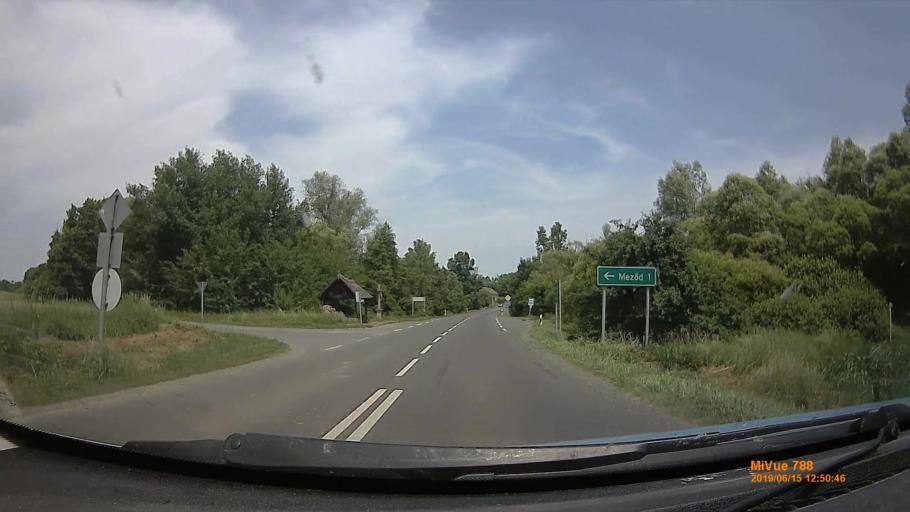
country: HU
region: Baranya
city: Sasd
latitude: 46.2783
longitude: 18.1077
